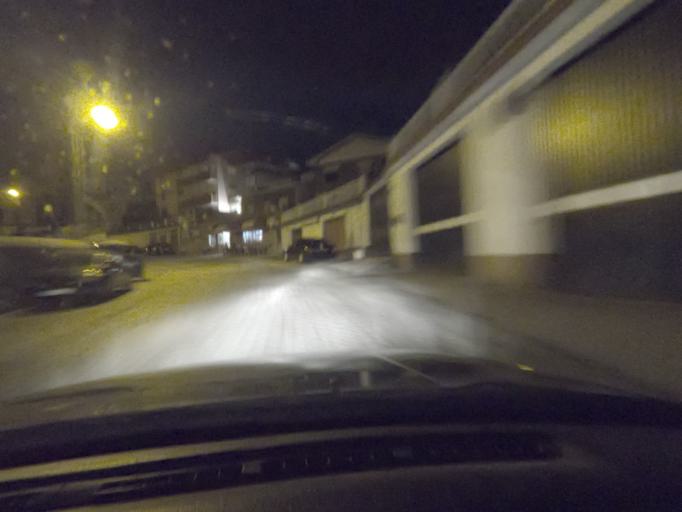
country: PT
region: Vila Real
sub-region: Peso da Regua
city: Peso da Regua
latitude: 41.1651
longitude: -7.7819
